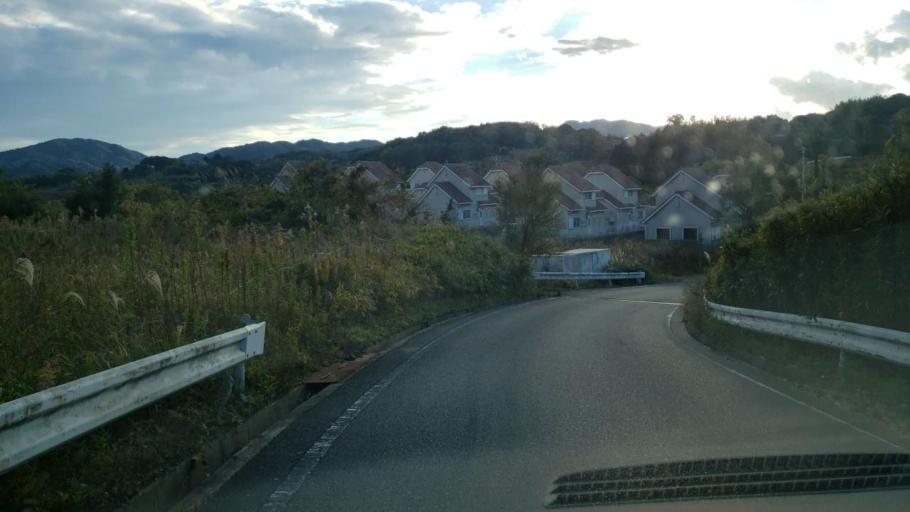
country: JP
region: Hyogo
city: Akashi
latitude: 34.5331
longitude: 134.9491
